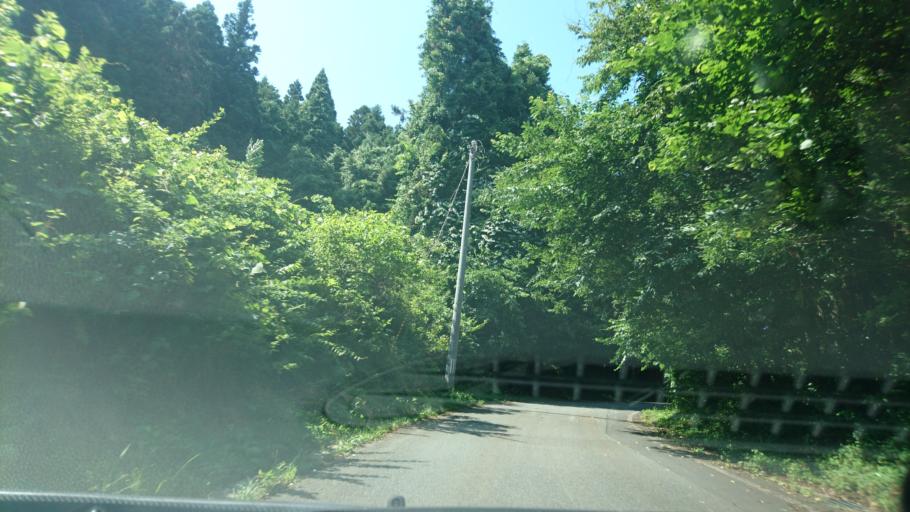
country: JP
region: Iwate
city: Ichinoseki
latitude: 38.9695
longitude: 141.1950
